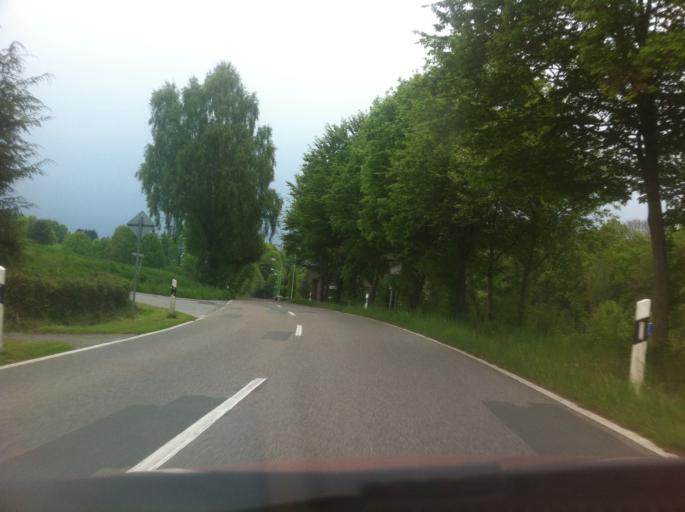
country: DE
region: North Rhine-Westphalia
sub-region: Regierungsbezirk Detmold
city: Rodinghausen
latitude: 52.2575
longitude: 8.5187
